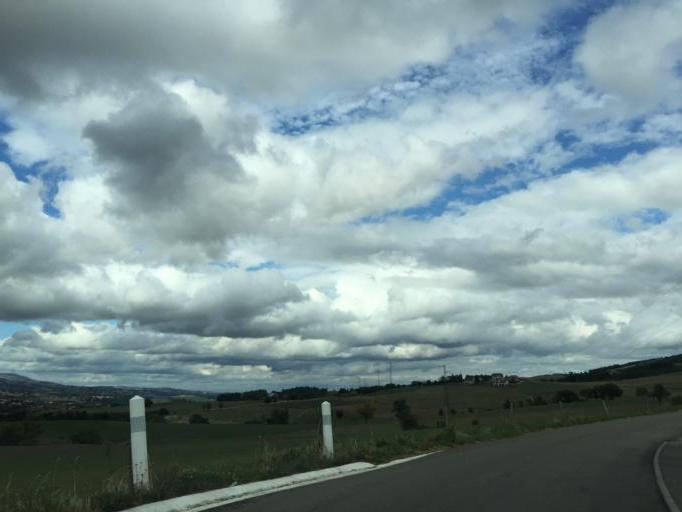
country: FR
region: Rhone-Alpes
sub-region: Departement de la Loire
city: Saint-Chamond
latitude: 45.4692
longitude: 4.5410
